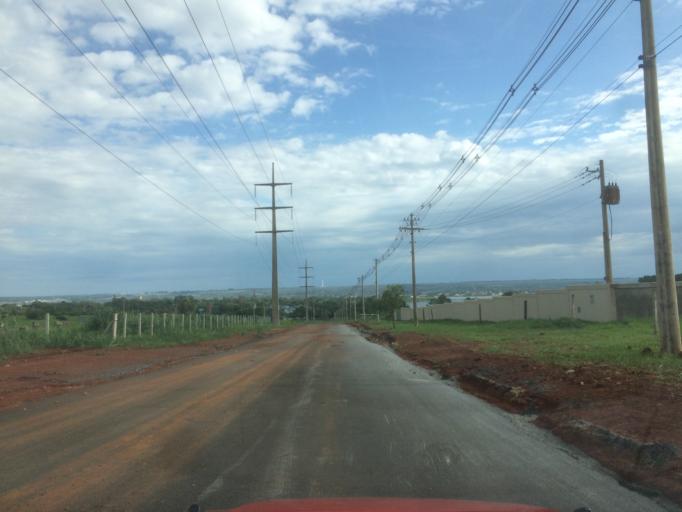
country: BR
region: Federal District
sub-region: Brasilia
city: Brasilia
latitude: -15.7911
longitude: -47.8613
